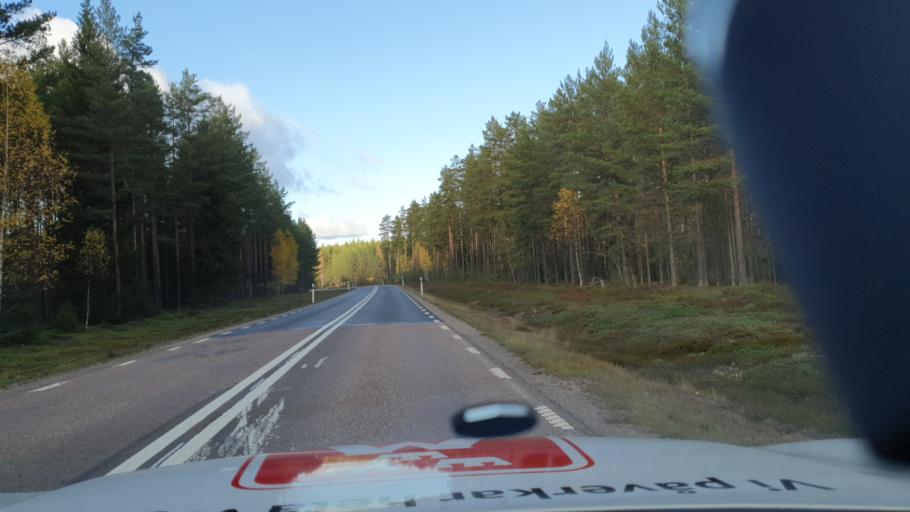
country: SE
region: Gaevleborg
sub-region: Gavle Kommun
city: Hedesunda
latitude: 60.4489
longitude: 16.9600
